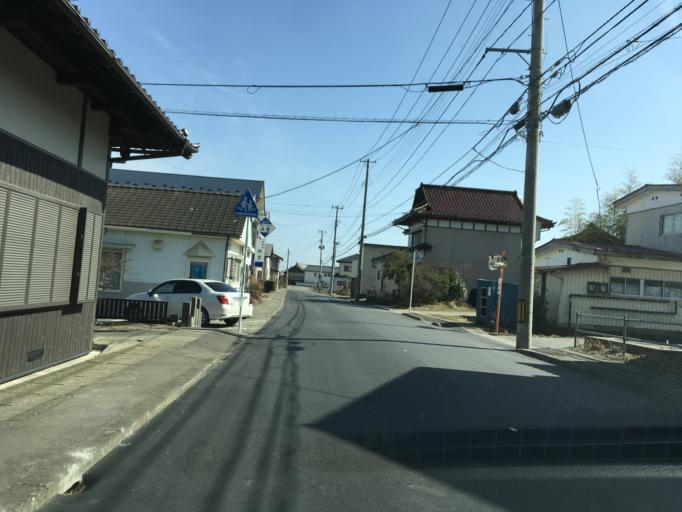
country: JP
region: Iwate
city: Ofunato
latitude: 38.8323
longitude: 141.5847
